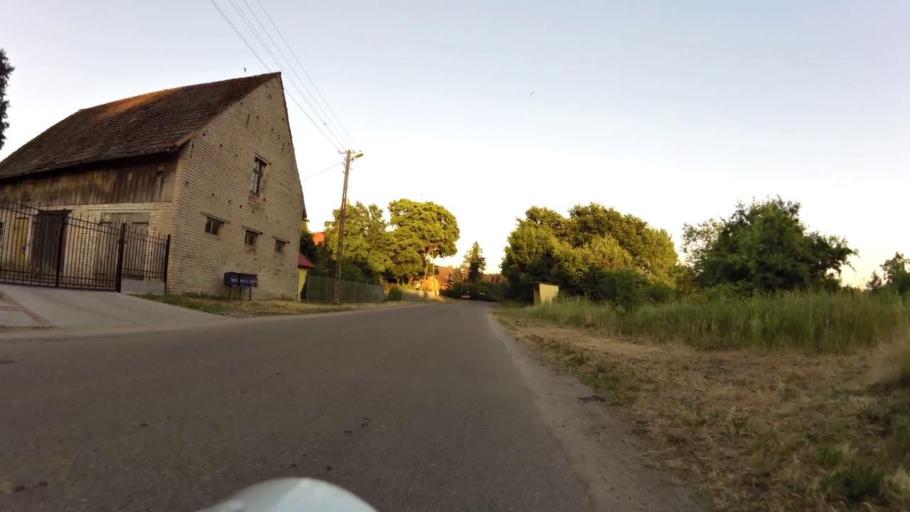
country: PL
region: West Pomeranian Voivodeship
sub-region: Powiat szczecinecki
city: Bialy Bor
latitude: 53.8625
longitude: 16.7529
